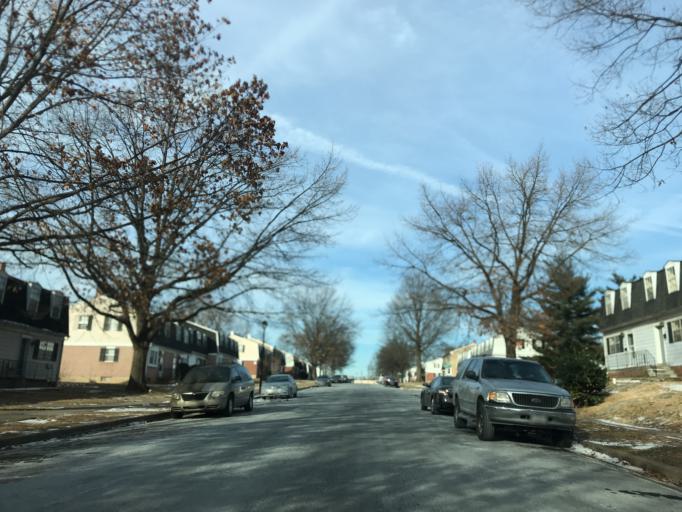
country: US
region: Maryland
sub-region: Baltimore County
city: Rosedale
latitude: 39.3283
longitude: -76.5290
